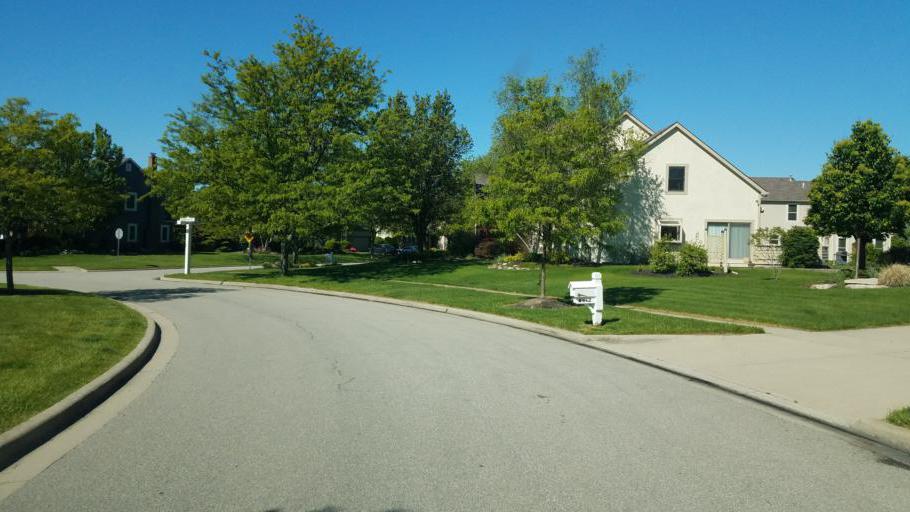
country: US
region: Ohio
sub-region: Franklin County
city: Westerville
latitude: 40.1744
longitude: -82.9357
